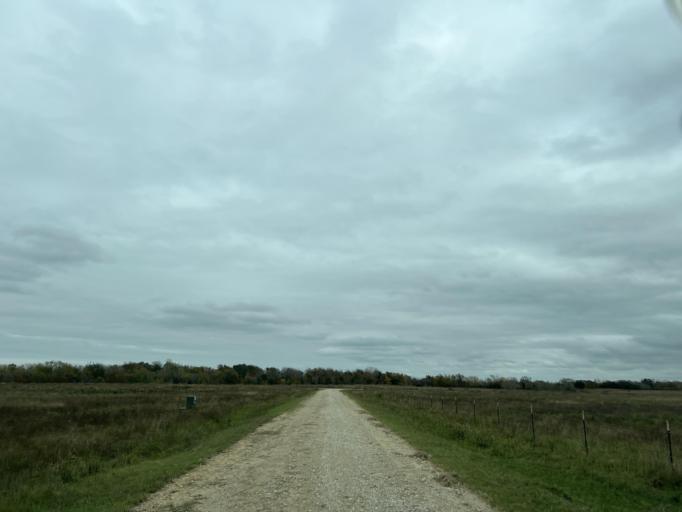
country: US
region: Texas
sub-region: Colorado County
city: Eagle Lake
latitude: 29.6706
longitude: -96.2746
